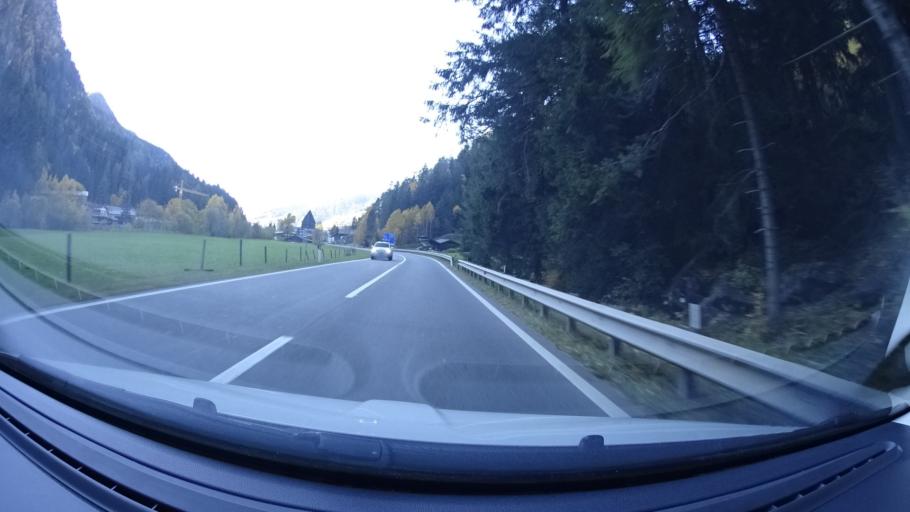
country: IT
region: Trentino-Alto Adige
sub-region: Bolzano
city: Ortisei
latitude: 46.5825
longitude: 11.6380
